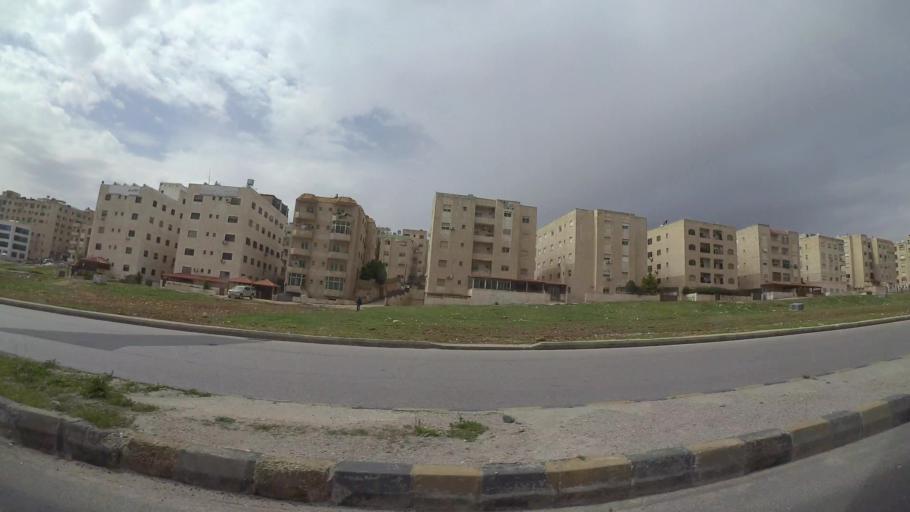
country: JO
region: Amman
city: Amman
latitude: 31.9841
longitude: 35.9180
